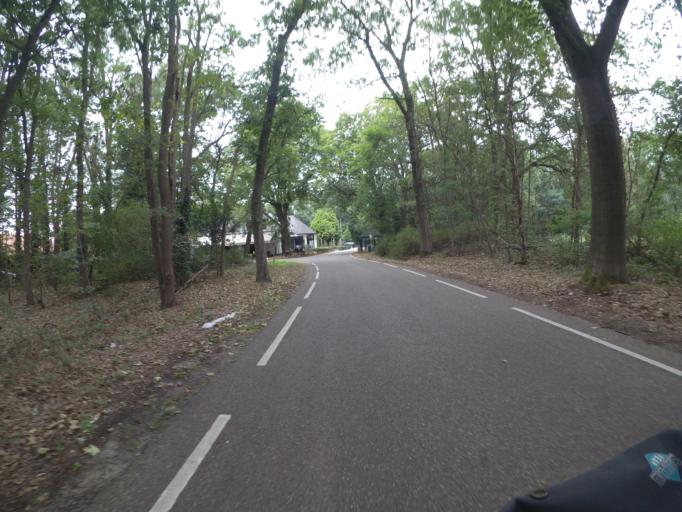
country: NL
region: North Brabant
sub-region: Gemeente Bernheze
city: Heesch
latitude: 51.7464
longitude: 5.5450
